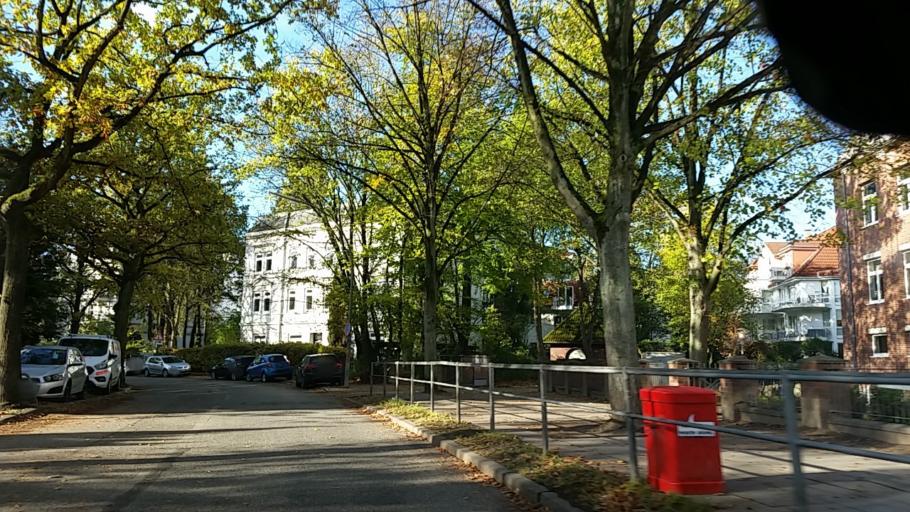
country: DE
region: Hamburg
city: Altona
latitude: 53.5680
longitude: 9.9086
